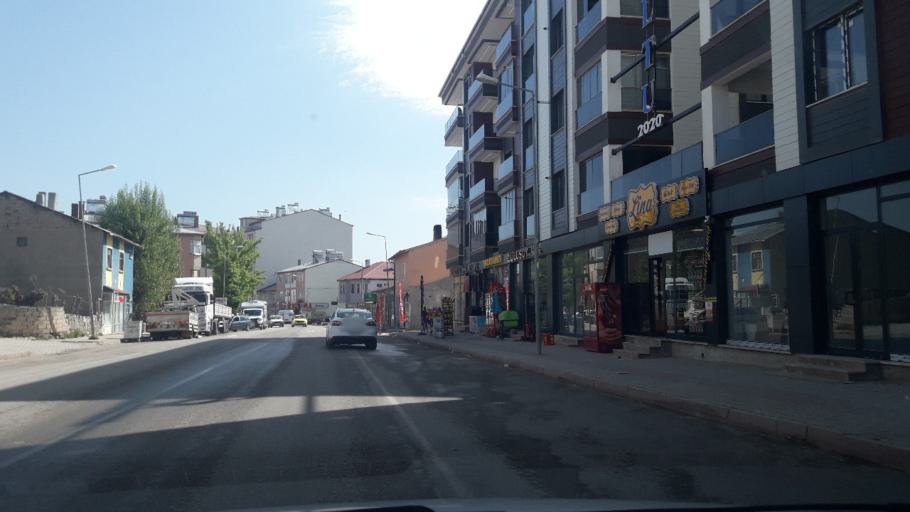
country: TR
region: Sivas
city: Kangal
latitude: 39.2324
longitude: 37.3894
